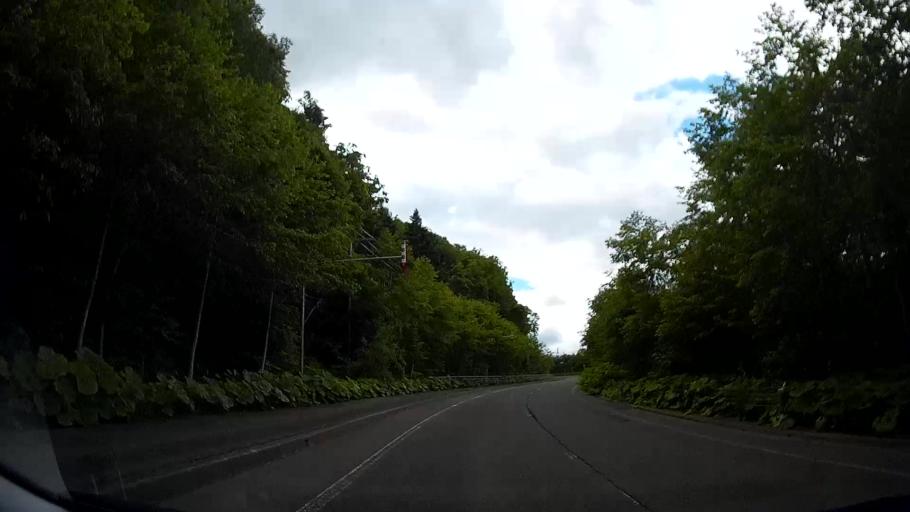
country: JP
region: Hokkaido
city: Kitahiroshima
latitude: 42.8450
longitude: 141.4571
